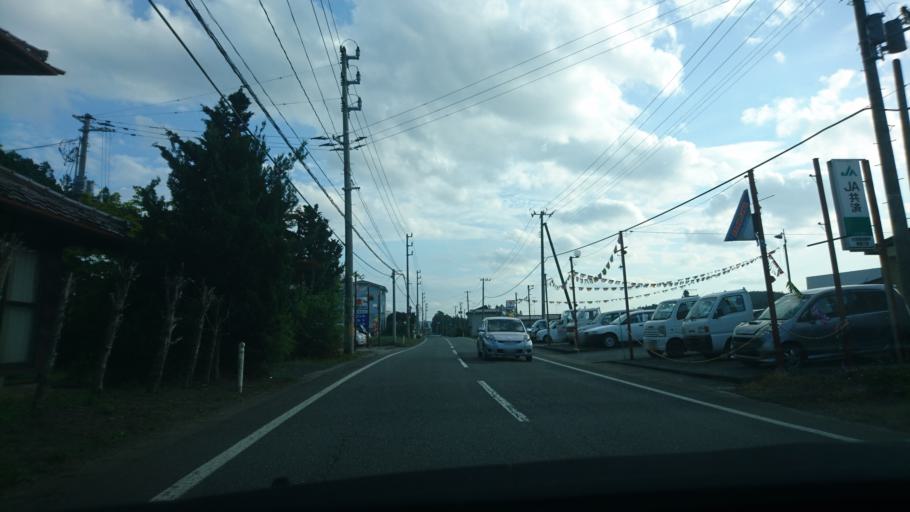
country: JP
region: Iwate
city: Mizusawa
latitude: 39.0318
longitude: 141.2953
